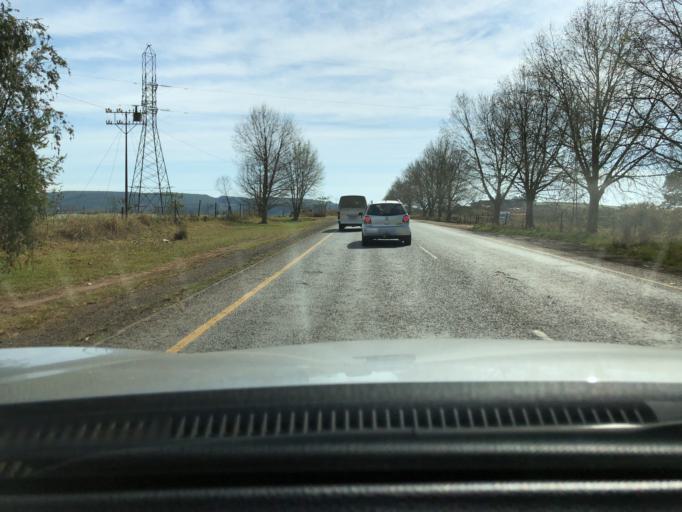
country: ZA
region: KwaZulu-Natal
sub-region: Sisonke District Municipality
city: Ixopo
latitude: -30.1270
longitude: 30.0818
